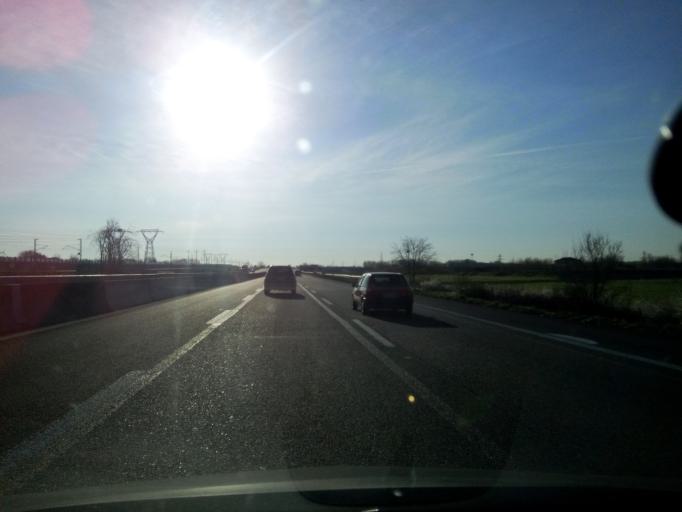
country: IT
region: Emilia-Romagna
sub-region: Provincia di Parma
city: Baganzola
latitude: 44.8495
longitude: 10.2989
